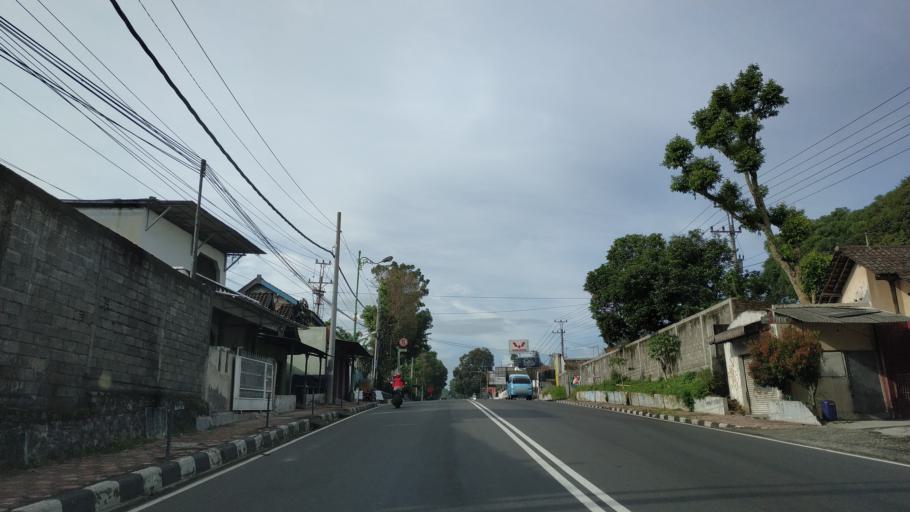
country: ID
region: Central Java
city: Salatiga
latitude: -7.3488
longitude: 110.5120
